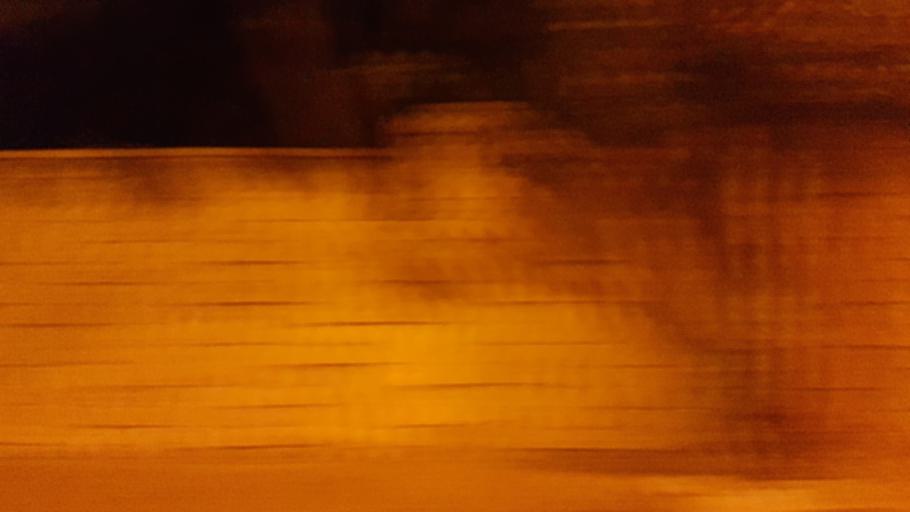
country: IL
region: Central District
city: Hod HaSharon
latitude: 32.1650
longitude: 34.8939
